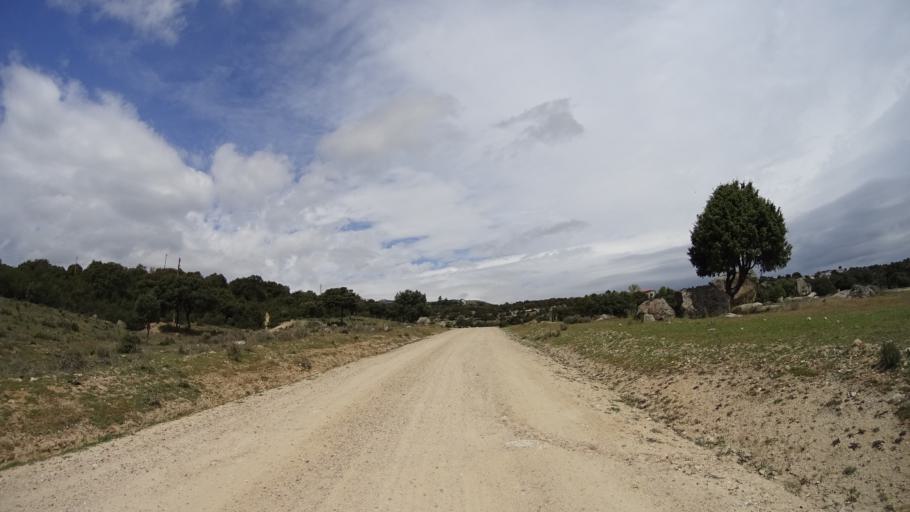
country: ES
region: Madrid
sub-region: Provincia de Madrid
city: Hoyo de Manzanares
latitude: 40.6187
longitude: -3.8818
